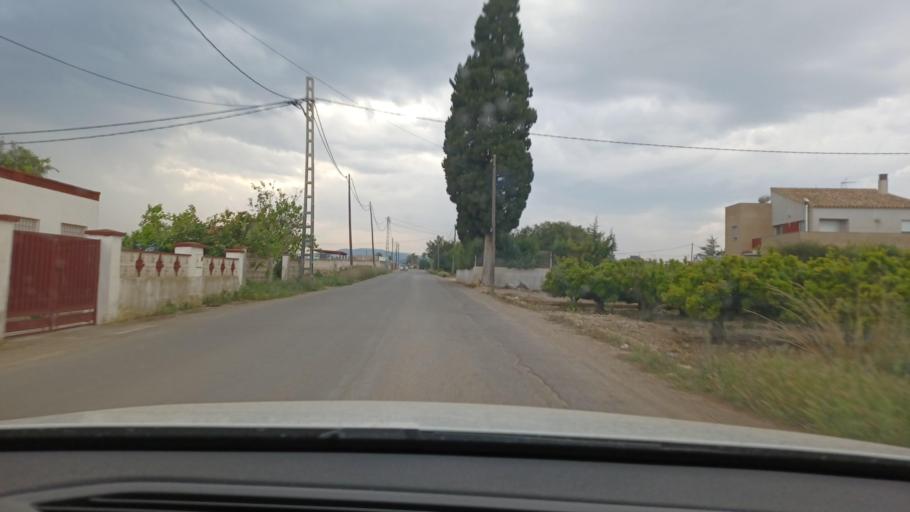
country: ES
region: Valencia
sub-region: Provincia de Castello
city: Benicarlo
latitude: 40.4045
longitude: 0.4059
